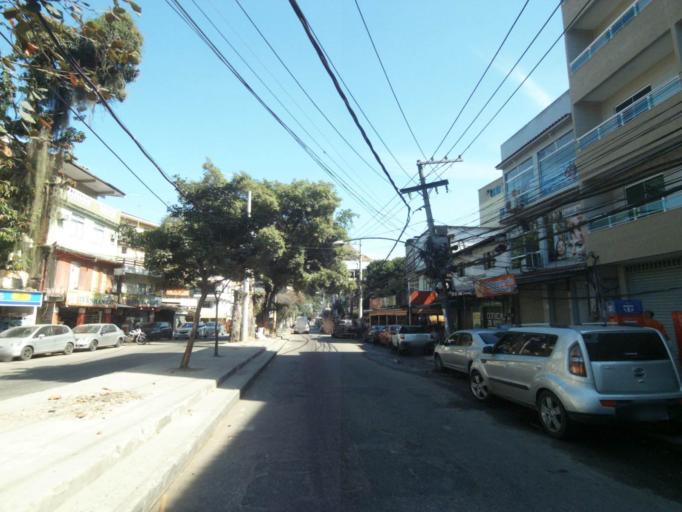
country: BR
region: Rio de Janeiro
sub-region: Rio De Janeiro
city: Rio de Janeiro
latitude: -22.9871
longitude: -43.3083
